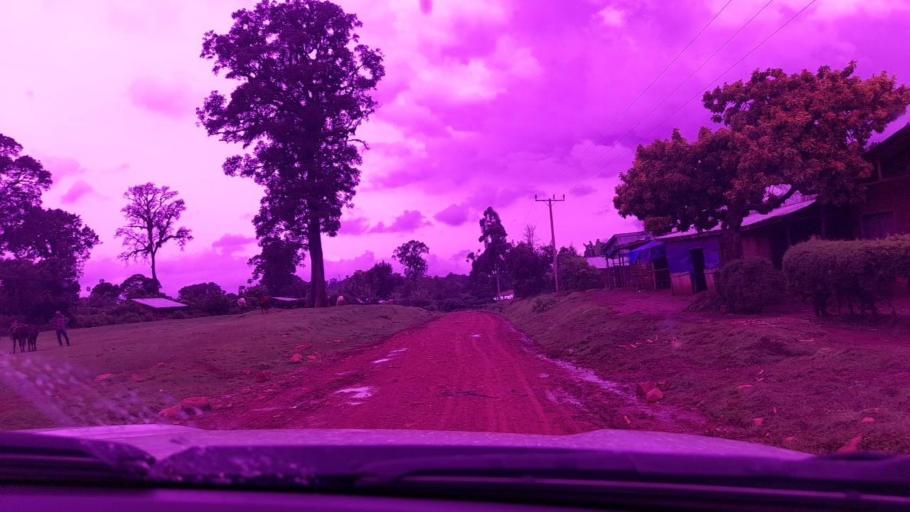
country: ET
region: Southern Nations, Nationalities, and People's Region
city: Tippi
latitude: 7.5805
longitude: 35.6302
